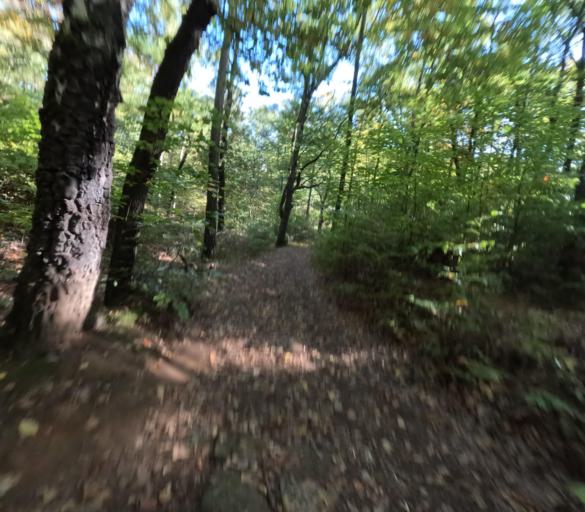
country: DE
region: Saxony
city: Radebeul
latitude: 51.1199
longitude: 13.6503
